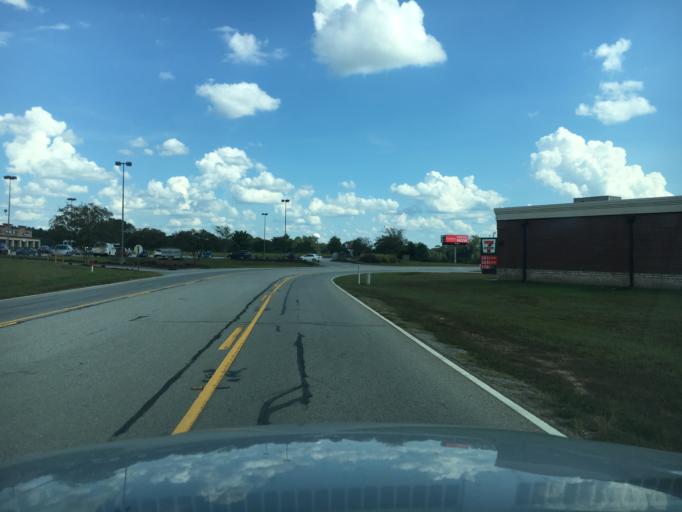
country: US
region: South Carolina
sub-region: Pickens County
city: Clemson
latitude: 34.6969
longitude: -82.8789
